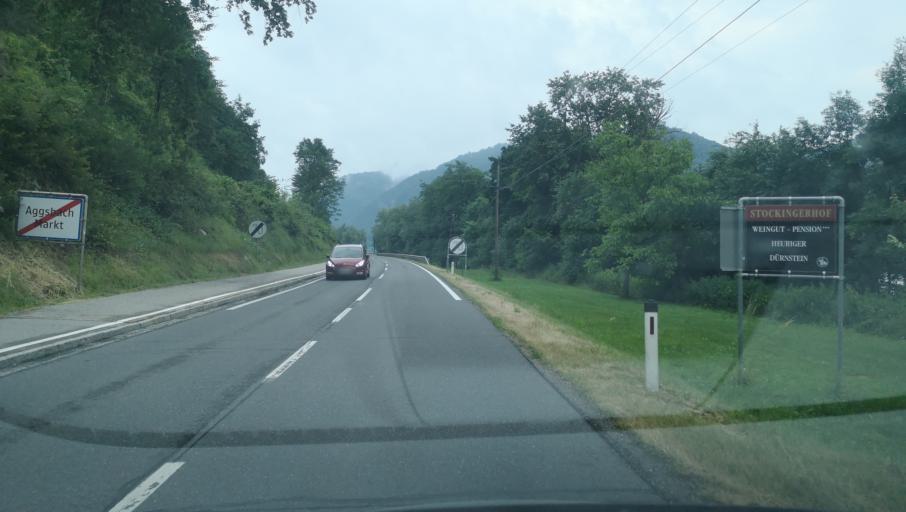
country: AT
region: Lower Austria
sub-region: Politischer Bezirk Krems
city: Aggsbach
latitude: 48.3014
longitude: 15.4057
